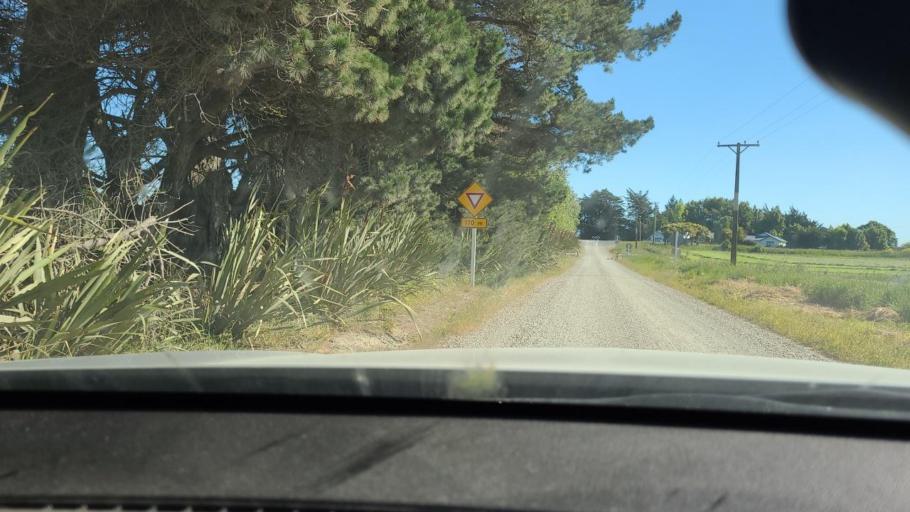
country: NZ
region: Southland
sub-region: Invercargill City
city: Invercargill
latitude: -46.2957
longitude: 168.2022
